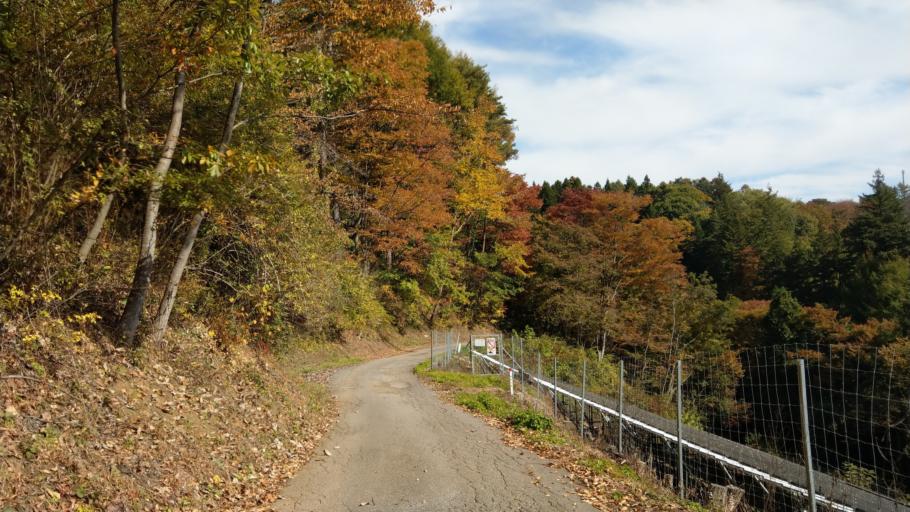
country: JP
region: Nagano
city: Komoro
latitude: 36.3553
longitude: 138.4431
